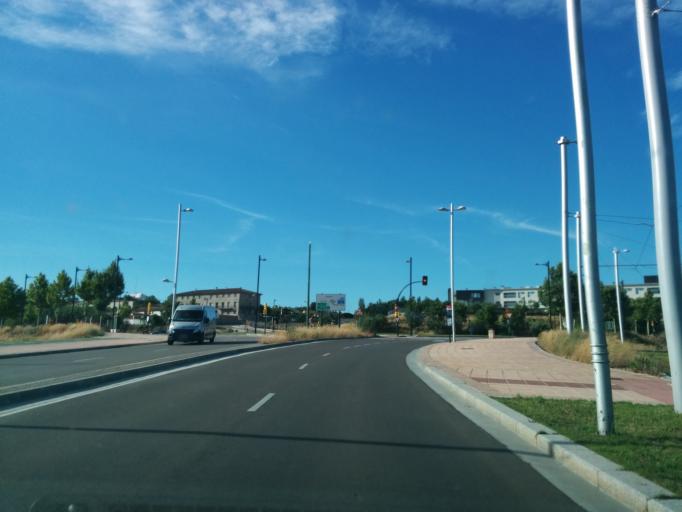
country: ES
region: Aragon
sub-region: Provincia de Zaragoza
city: Almozara
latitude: 41.6860
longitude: -0.8897
